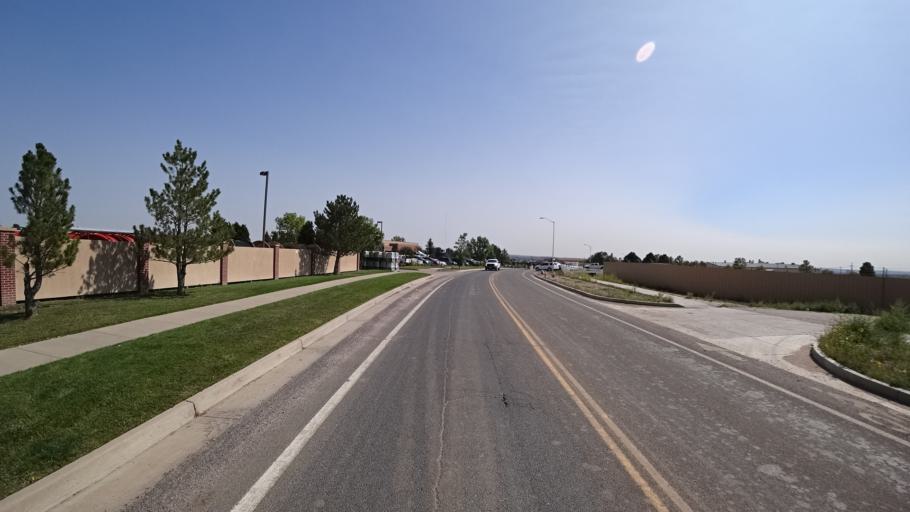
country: US
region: Colorado
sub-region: El Paso County
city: Colorado Springs
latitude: 38.8257
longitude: -104.8479
